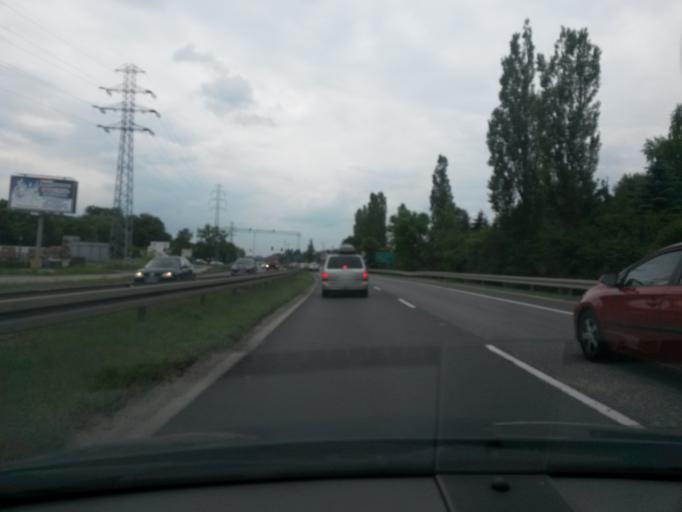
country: PL
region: Masovian Voivodeship
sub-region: Powiat pruszkowski
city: Nadarzyn
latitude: 52.0952
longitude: 20.8129
